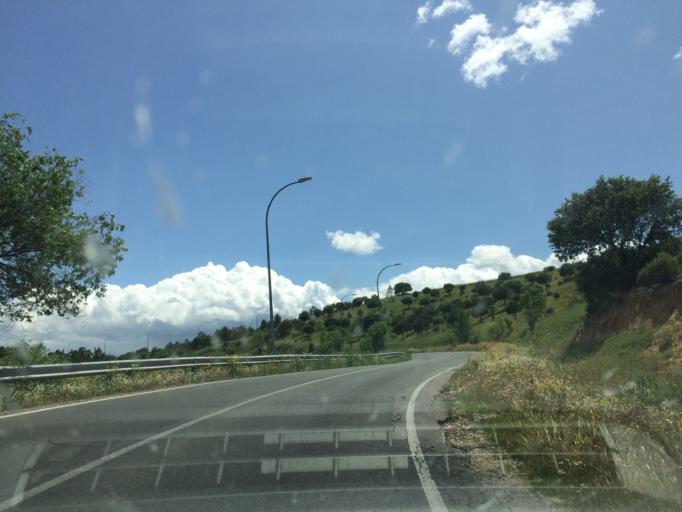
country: ES
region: Madrid
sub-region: Provincia de Madrid
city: Valdeolmos
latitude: 40.6942
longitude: -3.4441
